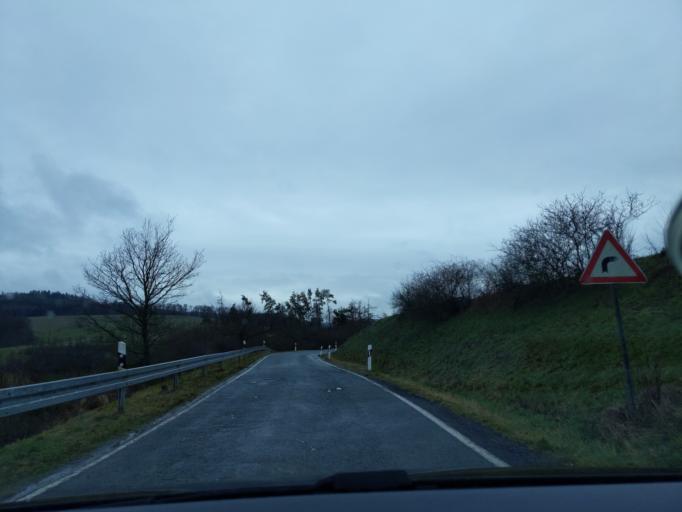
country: DE
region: Hesse
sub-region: Regierungsbezirk Kassel
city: Bad Arolsen
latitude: 51.3226
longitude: 9.0193
